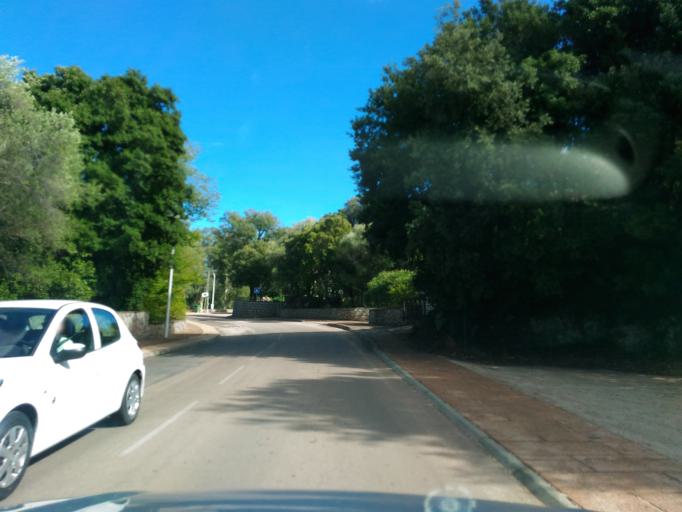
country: FR
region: Corsica
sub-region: Departement de la Corse-du-Sud
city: Porto-Vecchio
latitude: 41.7005
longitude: 9.3444
